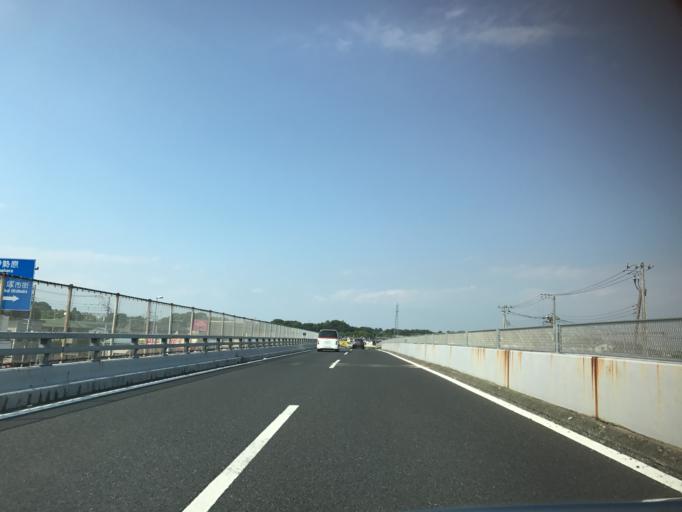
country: JP
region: Kanagawa
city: Isehara
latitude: 35.3691
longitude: 139.3112
